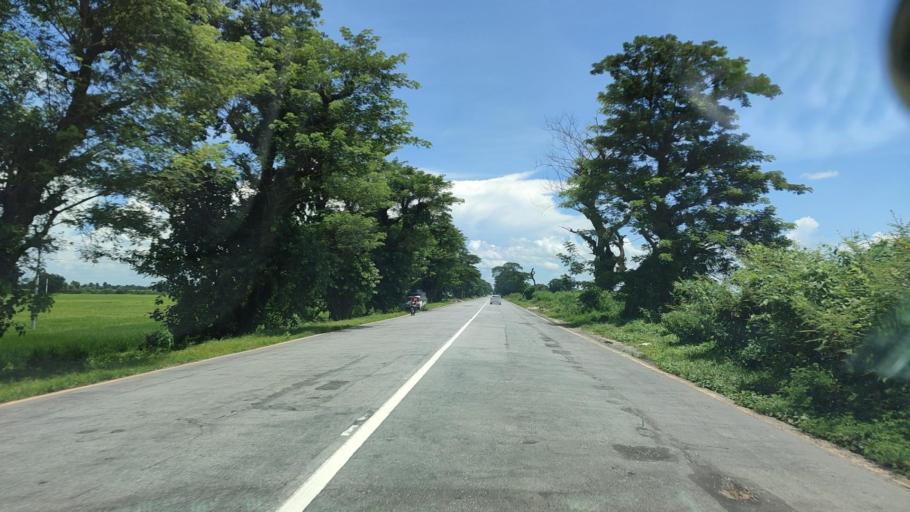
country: MM
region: Bago
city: Pyu
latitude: 18.2981
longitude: 96.5113
